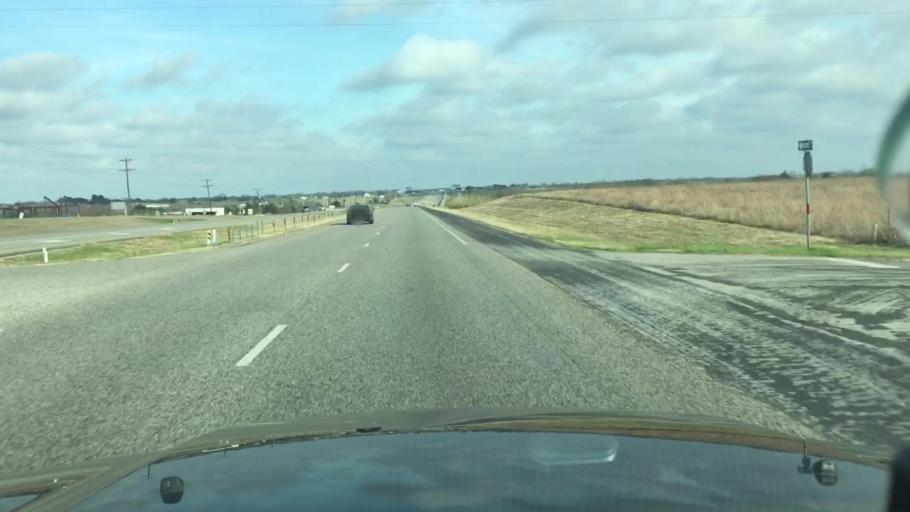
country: US
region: Texas
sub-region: Washington County
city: Brenham
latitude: 30.1385
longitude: -96.3172
